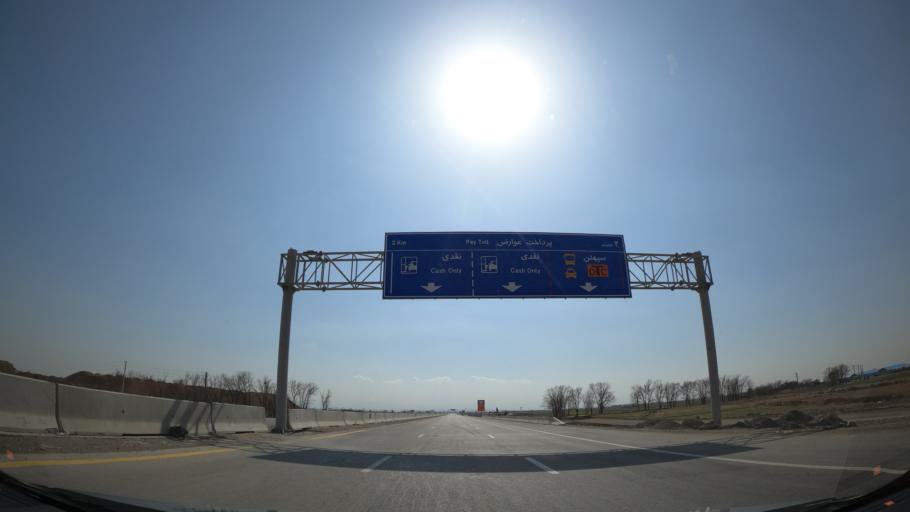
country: IR
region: Qazvin
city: Abyek
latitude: 35.9796
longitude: 50.4612
